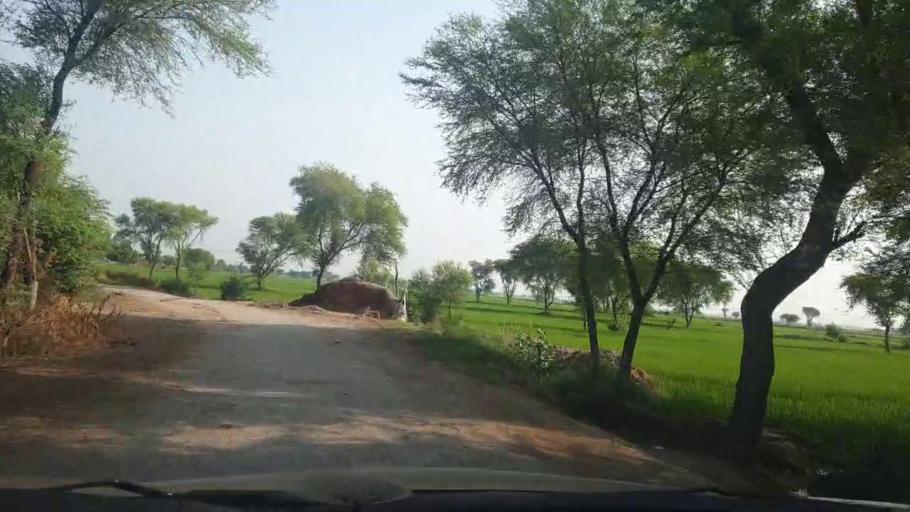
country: PK
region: Sindh
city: Larkana
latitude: 27.5885
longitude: 68.1611
